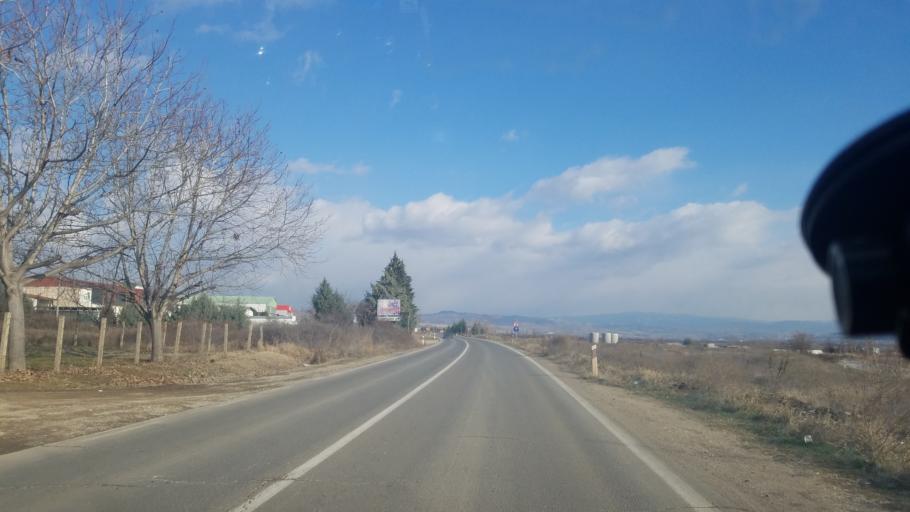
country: MK
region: Kocani
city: Kochani
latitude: 41.9001
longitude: 22.3829
